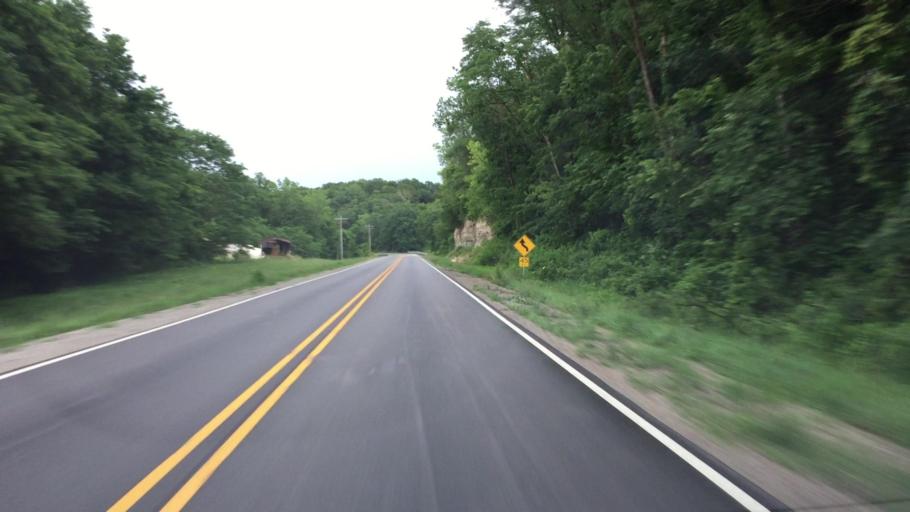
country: US
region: Iowa
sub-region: Lee County
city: Keokuk
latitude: 40.3734
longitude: -91.3868
